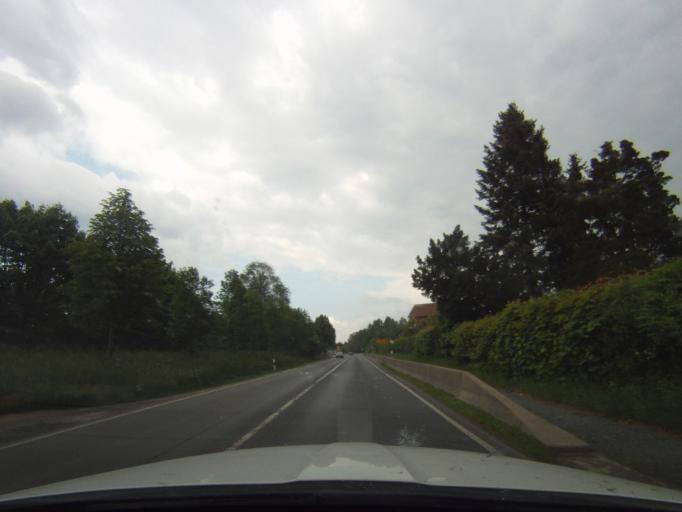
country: DE
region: Thuringia
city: Saalfeld
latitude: 50.6669
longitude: 11.3408
